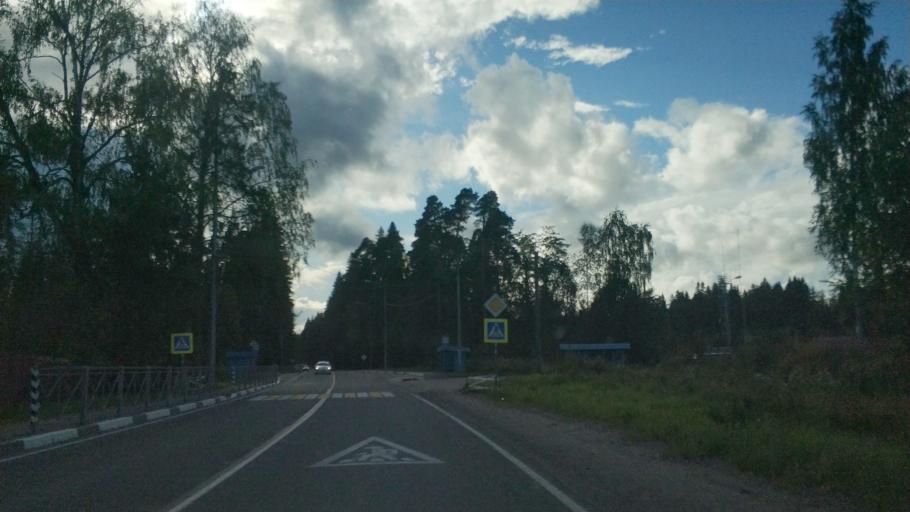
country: RU
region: Republic of Karelia
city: Lakhdenpokh'ya
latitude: 61.5159
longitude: 30.1321
